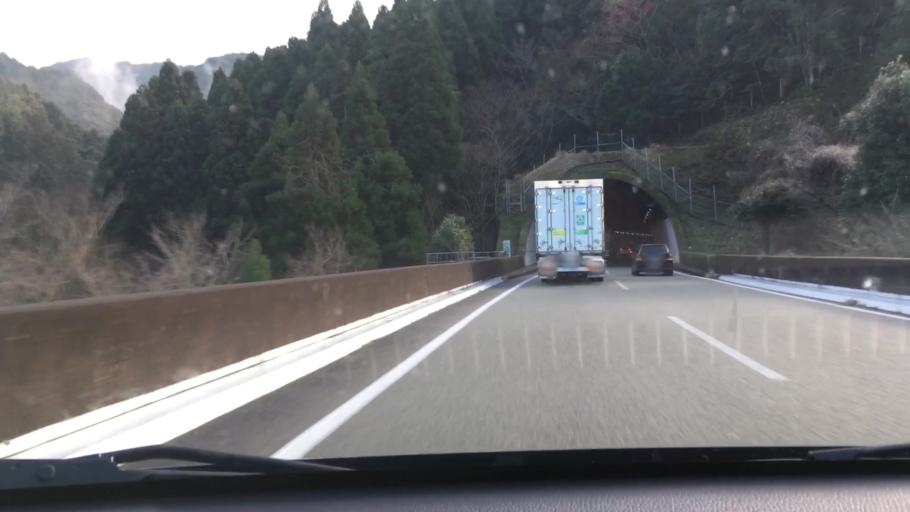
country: JP
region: Kumamoto
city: Hitoyoshi
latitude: 32.1345
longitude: 130.8040
